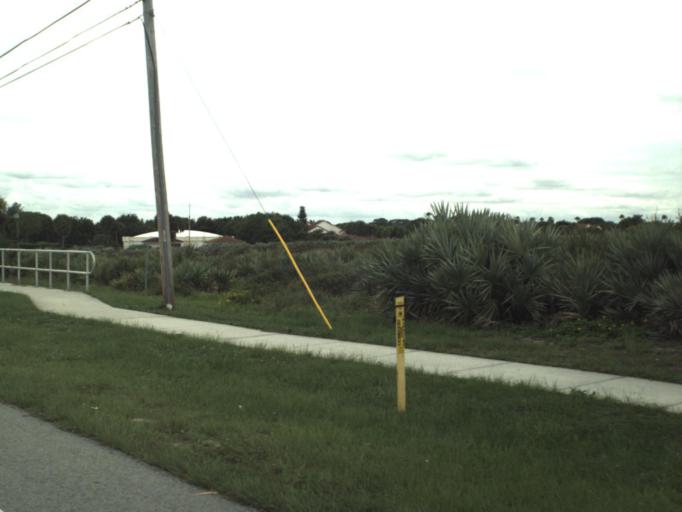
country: US
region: Florida
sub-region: Palm Beach County
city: Juno Beach
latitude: 26.8875
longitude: -80.0583
